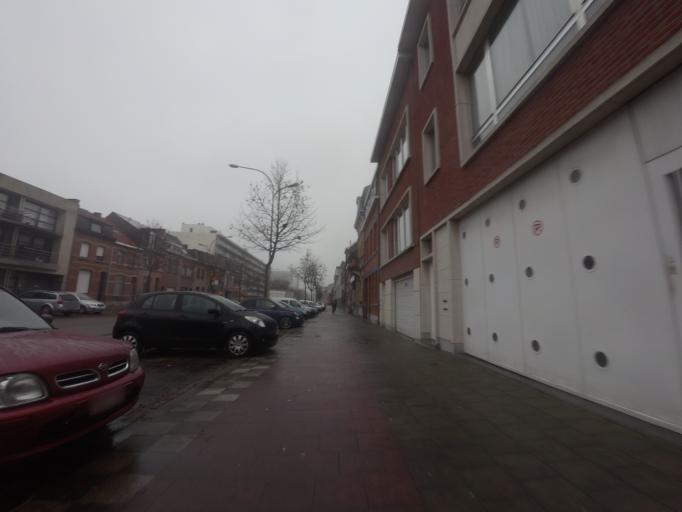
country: BE
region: Flanders
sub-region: Provincie Antwerpen
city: Hoboken
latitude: 51.1834
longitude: 4.3649
